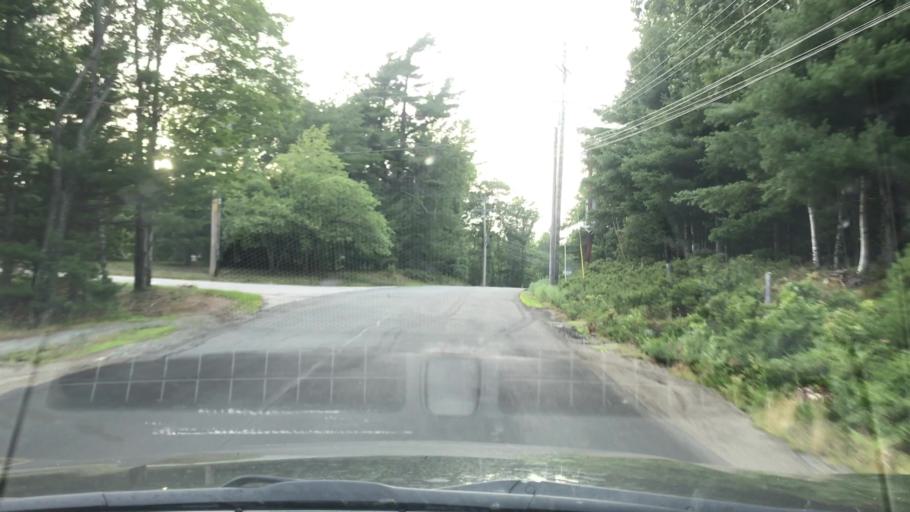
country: US
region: Maine
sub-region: Hancock County
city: Bar Harbor
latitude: 44.3665
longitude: -68.1937
